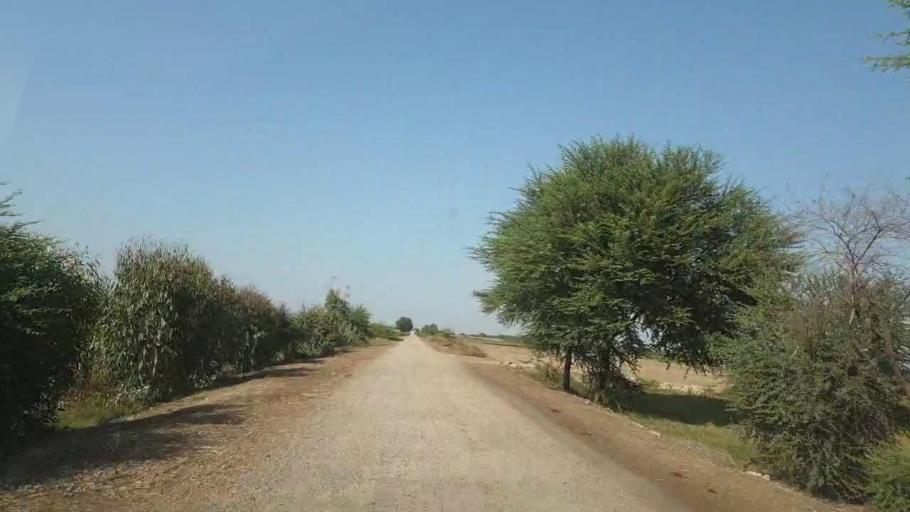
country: PK
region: Sindh
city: Nabisar
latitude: 25.0264
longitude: 69.4866
